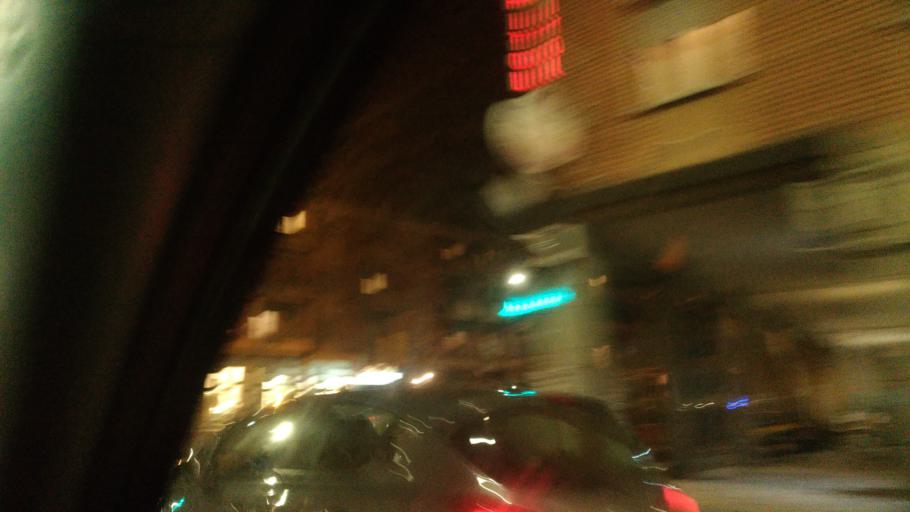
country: IT
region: Emilia-Romagna
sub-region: Provincia di Bologna
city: Bologna
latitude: 44.5309
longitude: 11.3528
